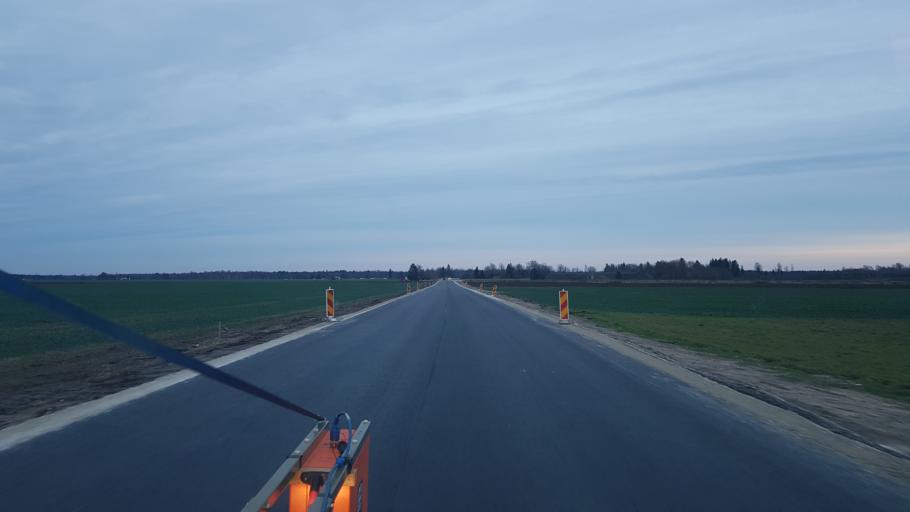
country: EE
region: Jogevamaa
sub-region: Jogeva linn
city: Jogeva
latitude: 58.7340
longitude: 26.2186
